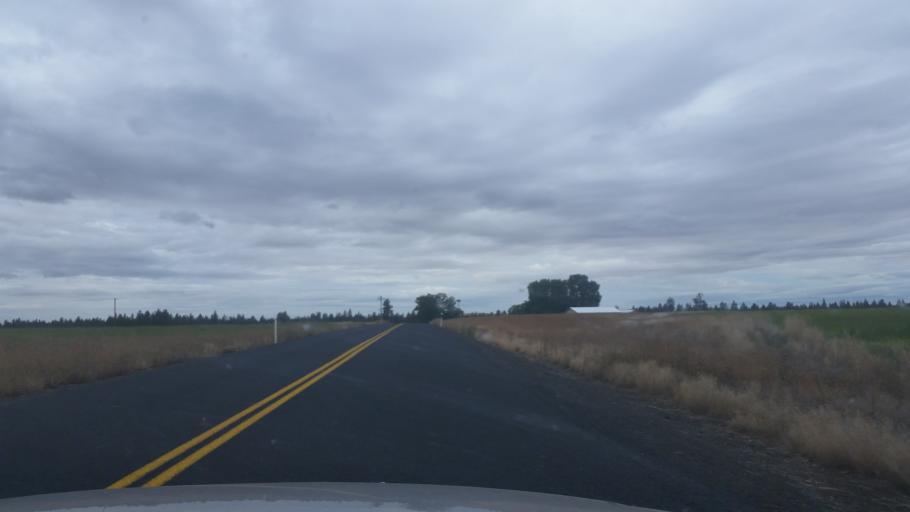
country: US
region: Washington
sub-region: Spokane County
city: Medical Lake
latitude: 47.5148
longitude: -117.7385
